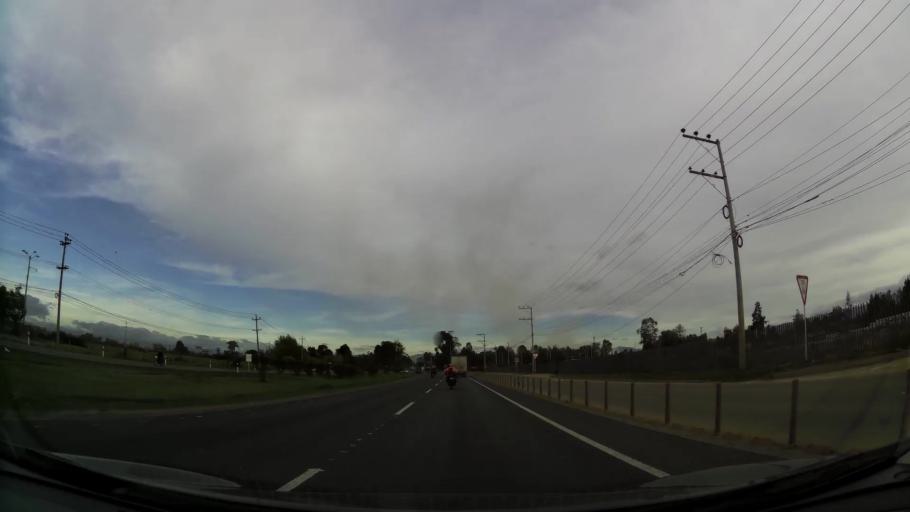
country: CO
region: Cundinamarca
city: Mosquera
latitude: 4.6975
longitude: -74.2195
